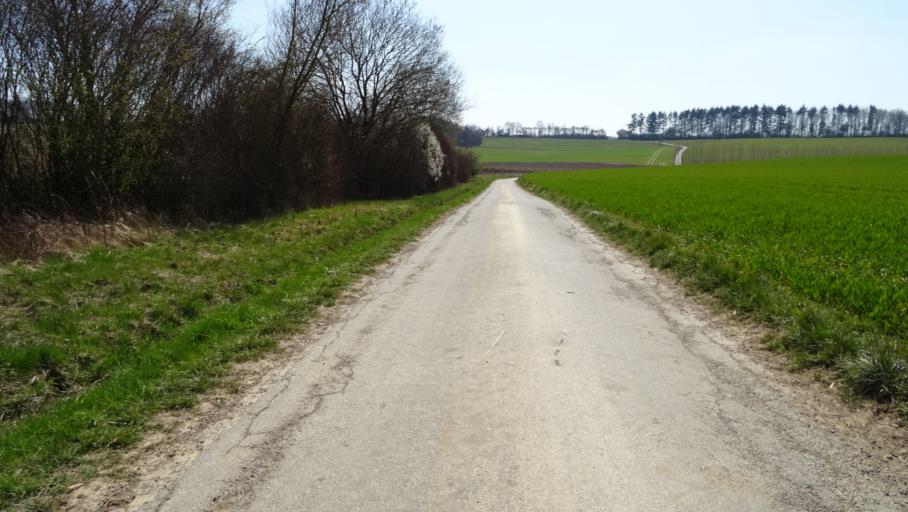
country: DE
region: Baden-Wuerttemberg
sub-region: Karlsruhe Region
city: Seckach
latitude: 49.4053
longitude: 9.2967
